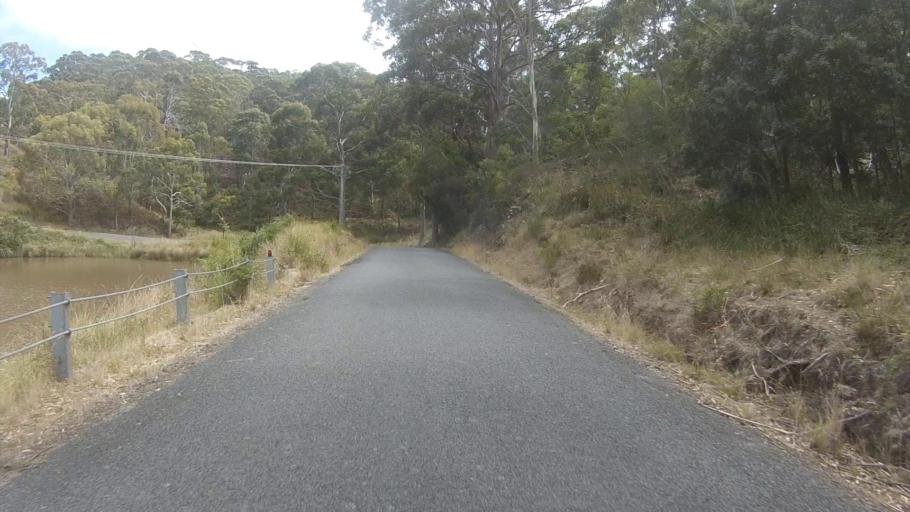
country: AU
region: Tasmania
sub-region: Kingborough
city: Blackmans Bay
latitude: -43.0548
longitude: 147.3285
